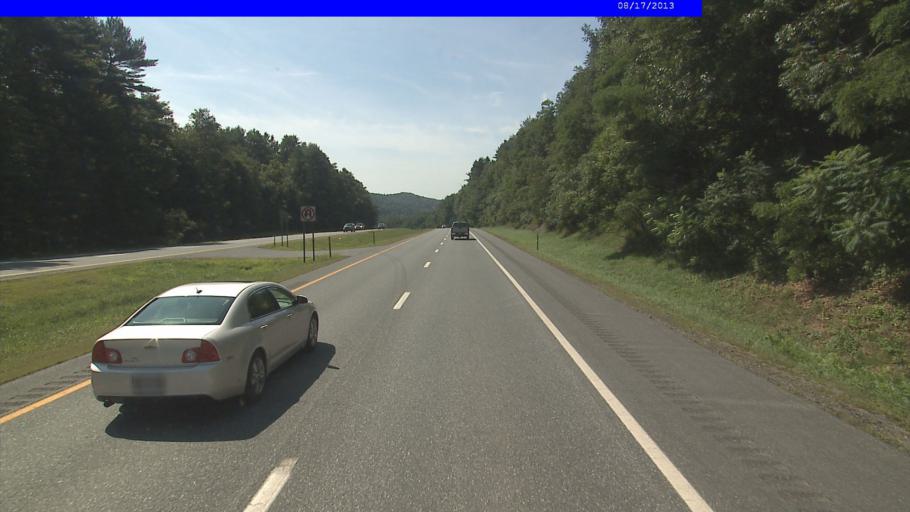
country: US
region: Vermont
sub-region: Windham County
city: West Brattleboro
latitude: 42.8614
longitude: -72.5810
